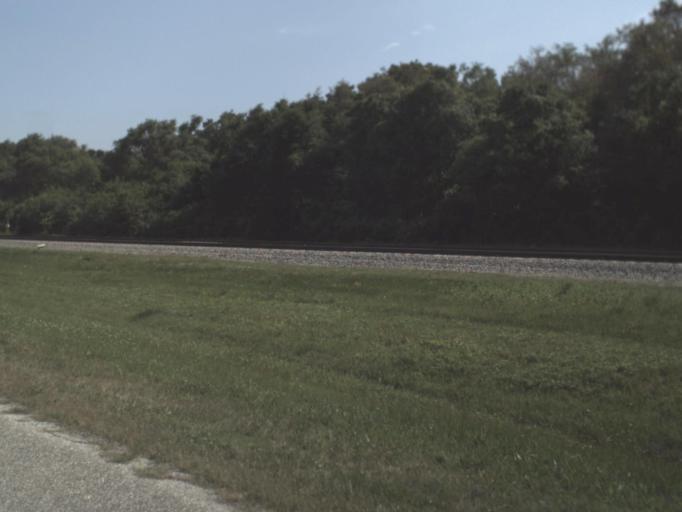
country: US
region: Florida
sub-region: Saint Johns County
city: Villano Beach
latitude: 29.9632
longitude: -81.3491
